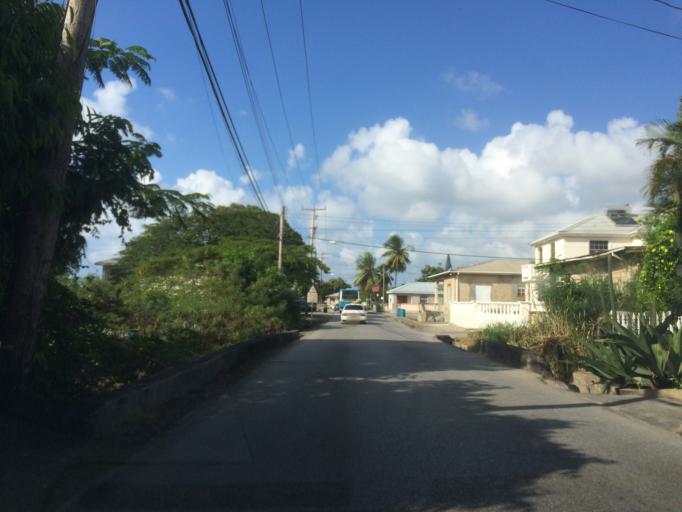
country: BB
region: Saint James
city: Holetown
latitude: 13.2161
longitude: -59.6410
